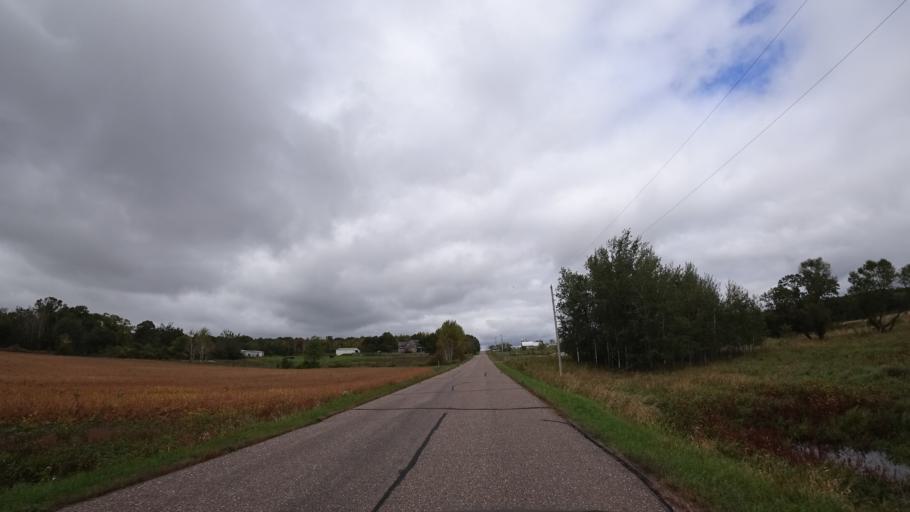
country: US
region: Wisconsin
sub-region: Chippewa County
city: Lake Wissota
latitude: 44.9869
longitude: -91.2868
